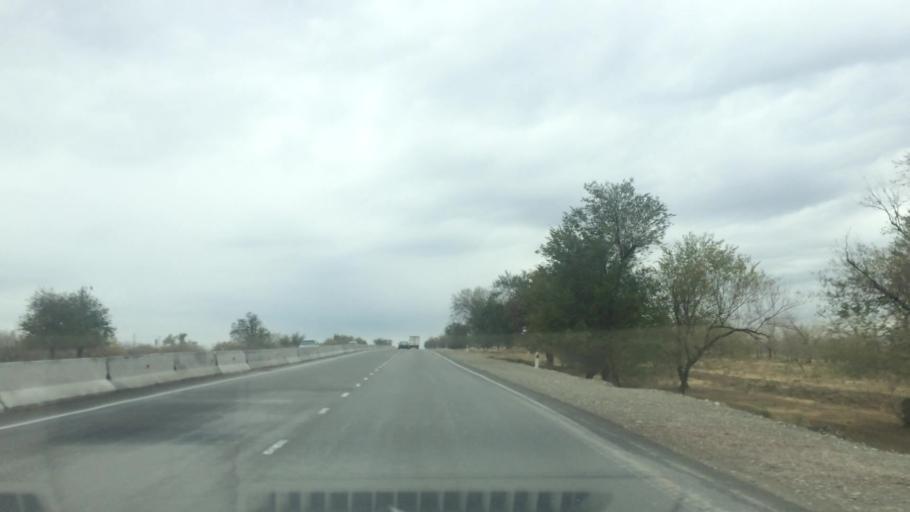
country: UZ
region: Samarqand
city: Bulung'ur
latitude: 39.9312
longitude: 67.5223
